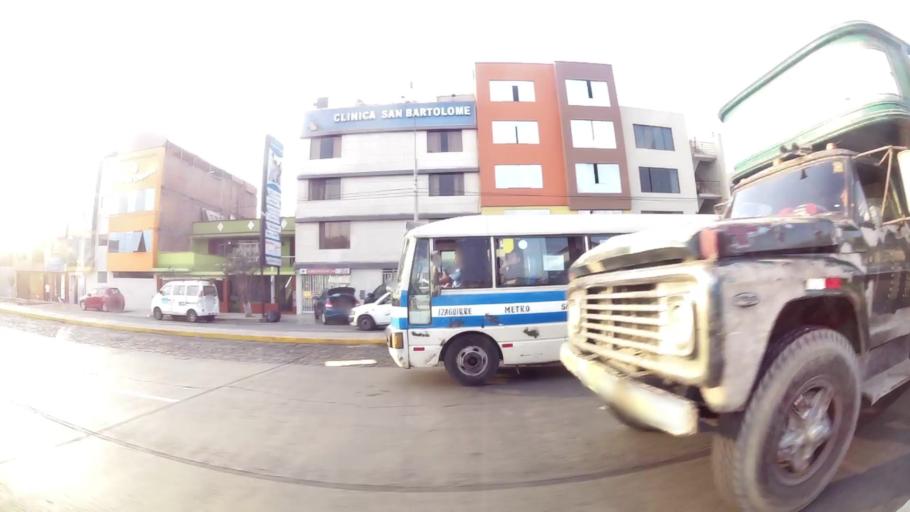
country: PE
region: Lima
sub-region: Lima
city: Independencia
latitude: -11.9916
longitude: -77.0755
